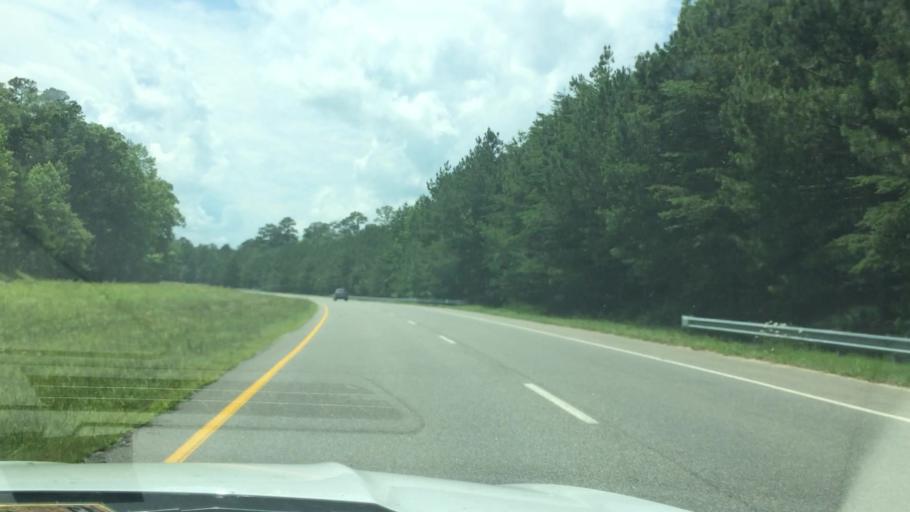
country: US
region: Virginia
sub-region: Middlesex County
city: Saluda
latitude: 37.5654
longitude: -76.6493
